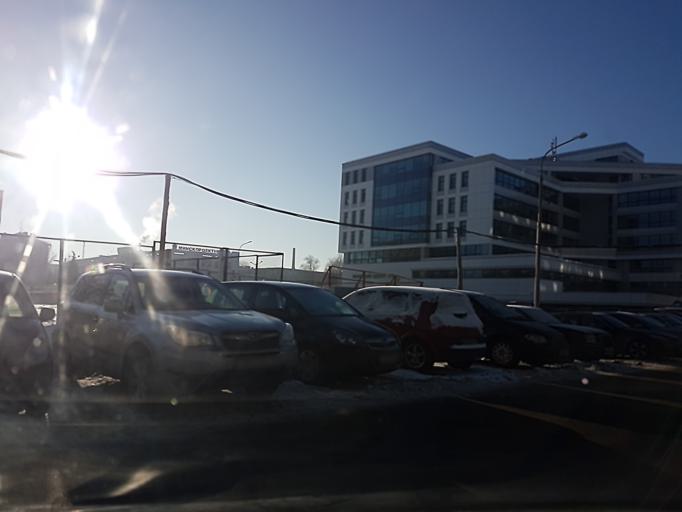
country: BY
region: Minsk
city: Minsk
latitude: 53.9086
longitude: 27.5180
